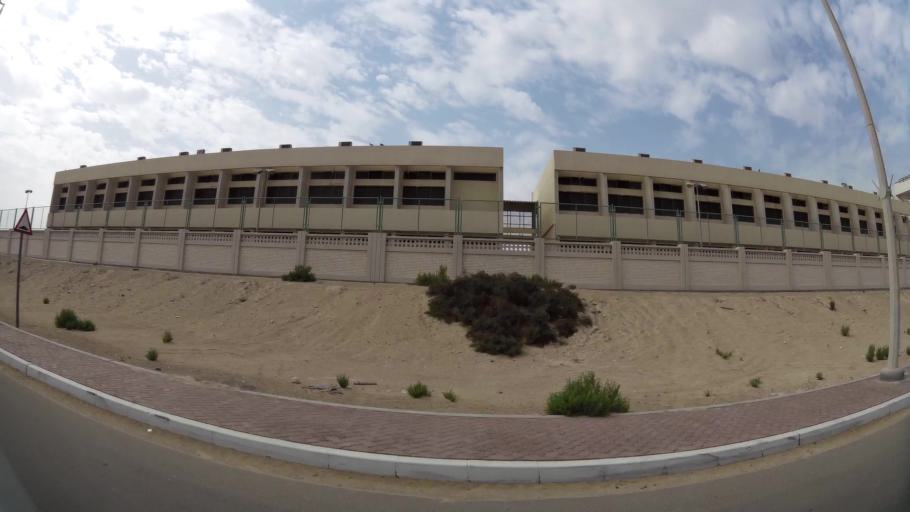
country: AE
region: Abu Dhabi
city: Abu Dhabi
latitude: 24.3162
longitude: 54.6441
